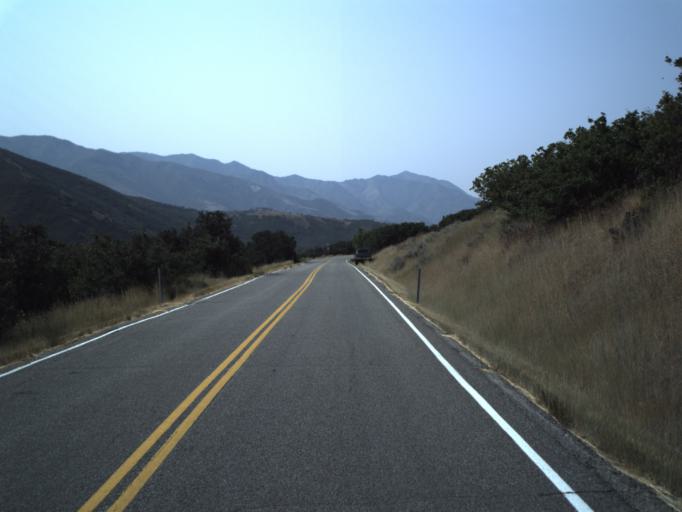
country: US
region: Utah
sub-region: Summit County
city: Summit Park
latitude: 40.7819
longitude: -111.6846
